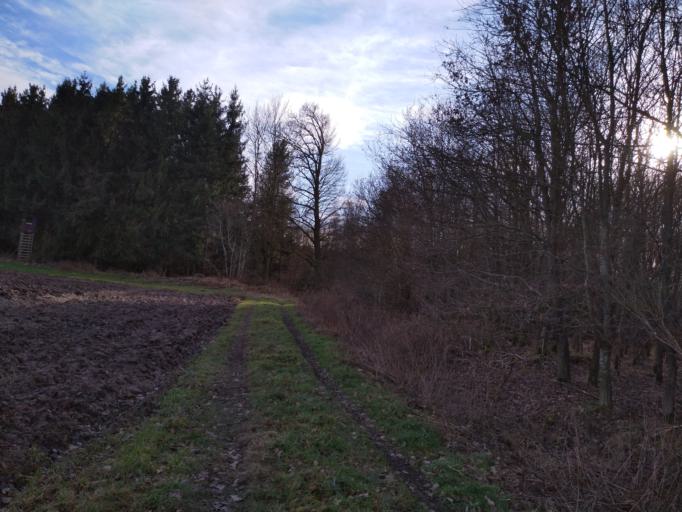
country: DE
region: Bavaria
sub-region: Swabia
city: Rettenbach
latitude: 48.4272
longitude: 10.3193
